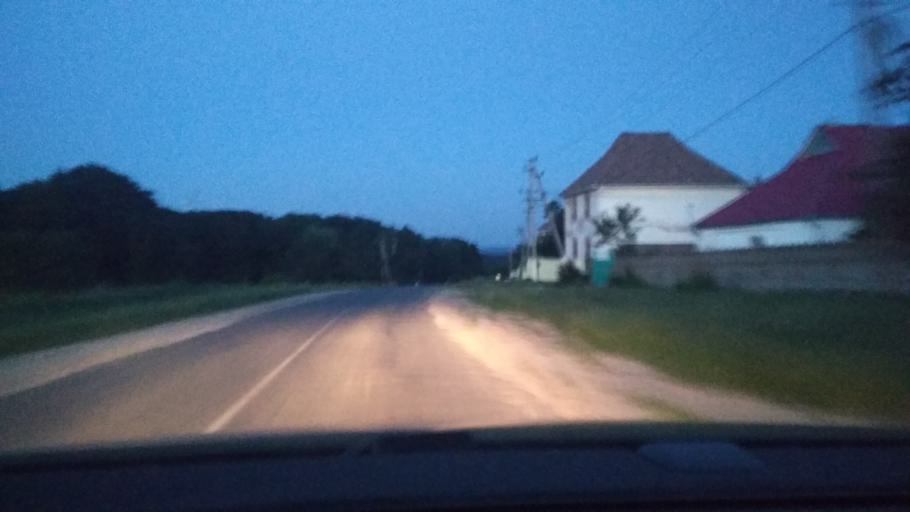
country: MD
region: Nisporeni
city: Nisporeni
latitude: 47.1563
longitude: 28.1904
